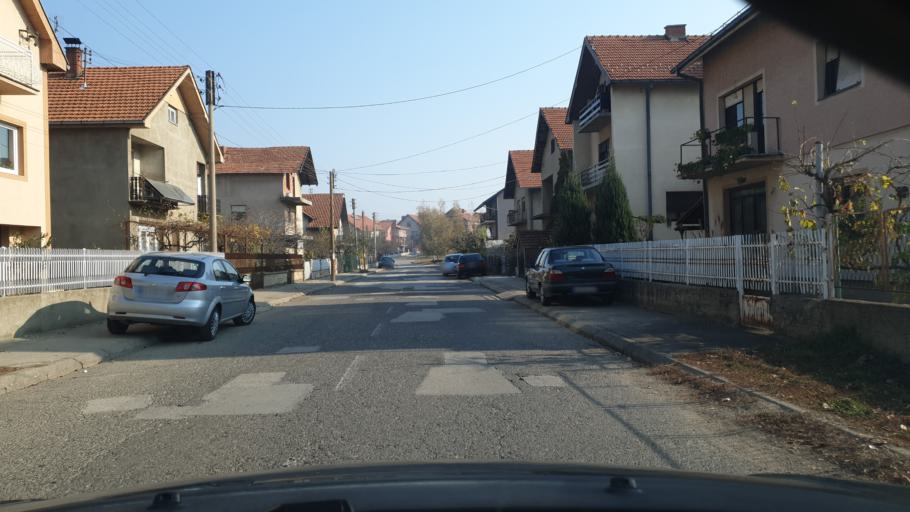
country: RS
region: Central Serbia
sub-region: Zajecarski Okrug
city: Zajecar
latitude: 43.9036
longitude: 22.2915
